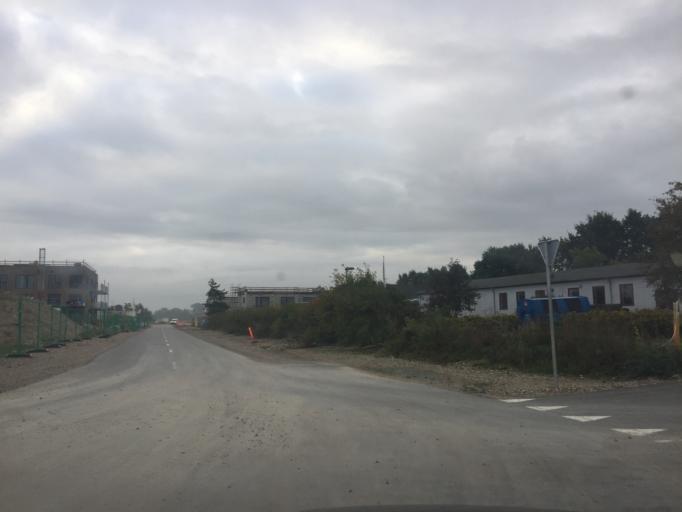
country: DK
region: Capital Region
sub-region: Hoje-Taastrup Kommune
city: Flong
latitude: 55.6448
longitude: 12.1996
